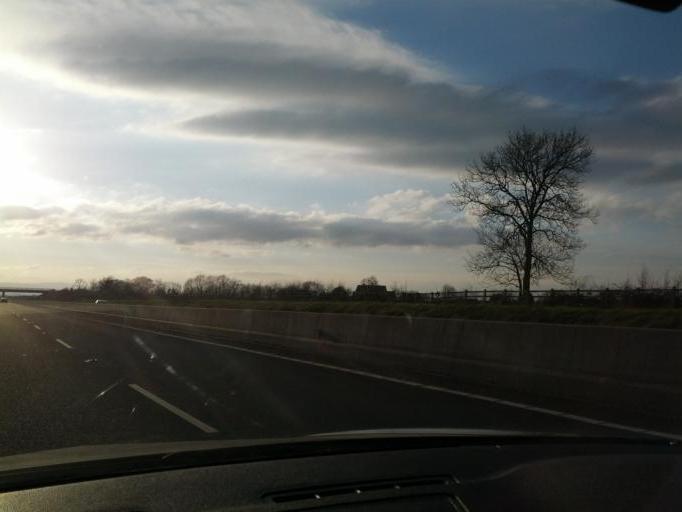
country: IE
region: Munster
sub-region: North Tipperary
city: Nenagh
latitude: 52.8663
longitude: -8.0893
